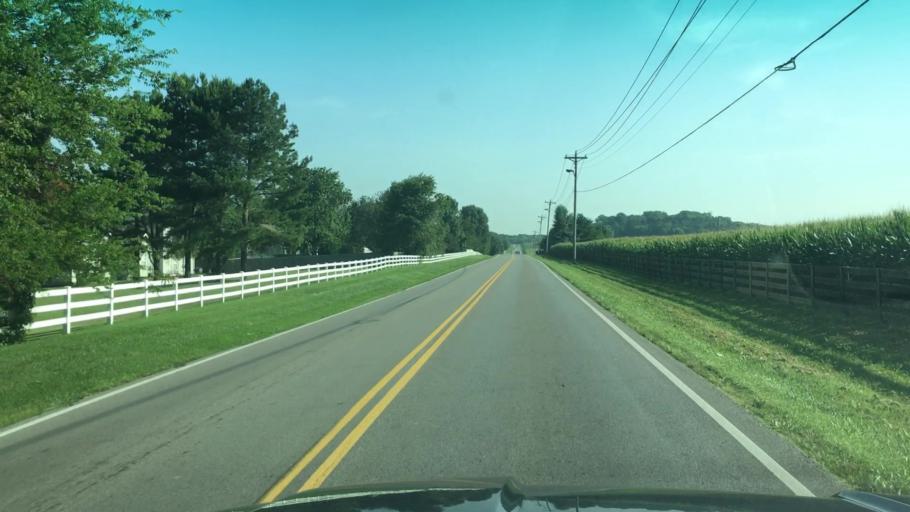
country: US
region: Tennessee
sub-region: Williamson County
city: Thompson's Station
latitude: 35.7802
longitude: -86.8792
